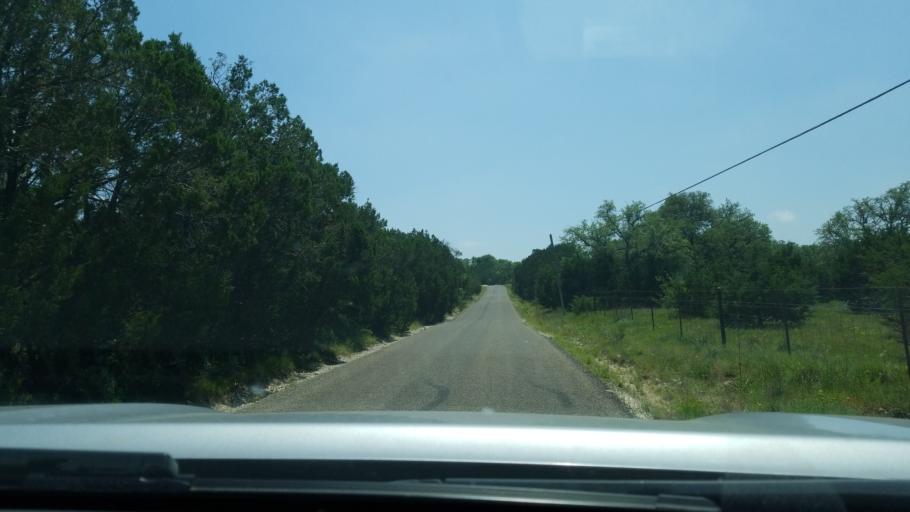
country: US
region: Texas
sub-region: Blanco County
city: Blanco
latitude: 30.0836
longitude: -98.4004
